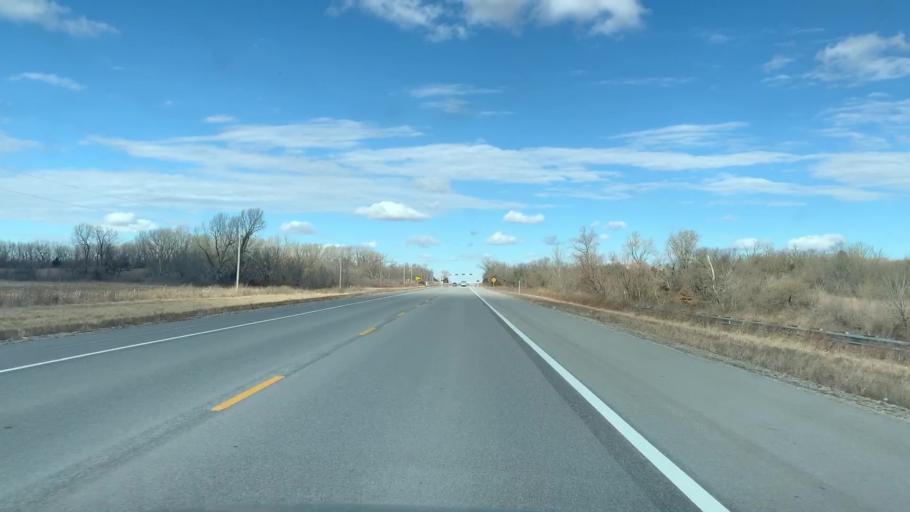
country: US
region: Kansas
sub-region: Cherokee County
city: Columbus
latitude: 37.3175
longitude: -94.8323
